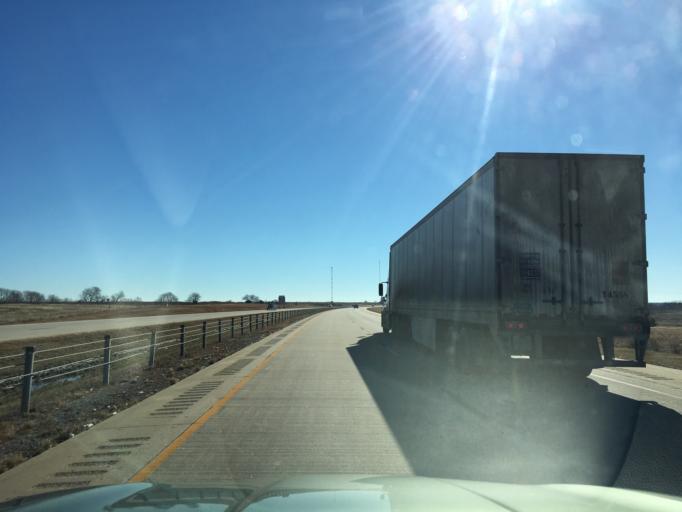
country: US
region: Oklahoma
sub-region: Kay County
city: Tonkawa
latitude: 36.5229
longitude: -97.3389
